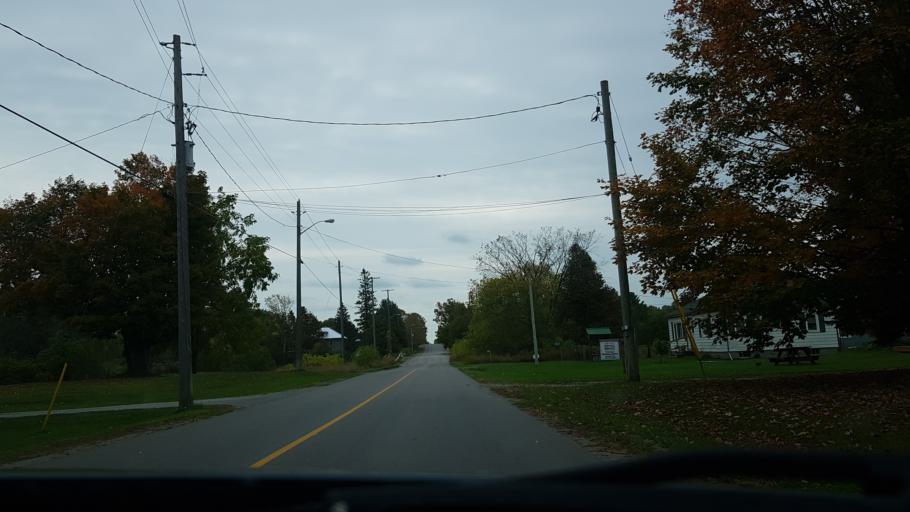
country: CA
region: Ontario
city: Orillia
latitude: 44.5986
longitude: -78.9408
